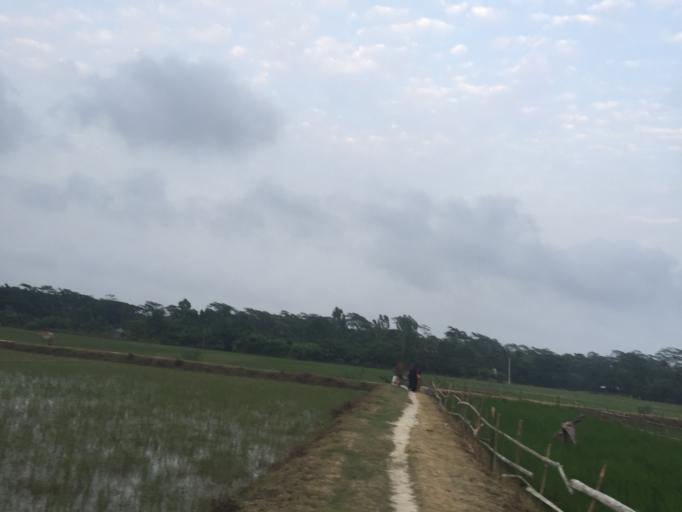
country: BD
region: Barisal
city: Mathba
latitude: 22.1927
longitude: 89.9346
